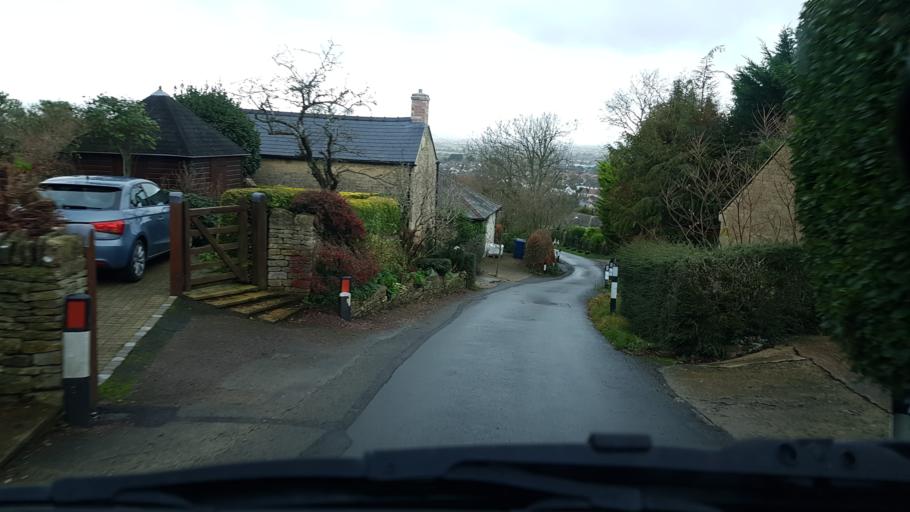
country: GB
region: England
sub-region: Gloucestershire
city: Gotherington
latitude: 51.9478
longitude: -2.0367
